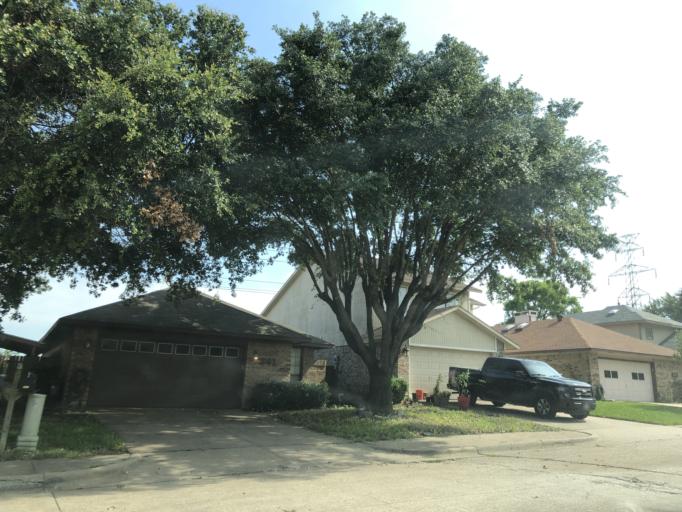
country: US
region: Texas
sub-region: Dallas County
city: Sunnyvale
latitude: 32.8322
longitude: -96.6084
